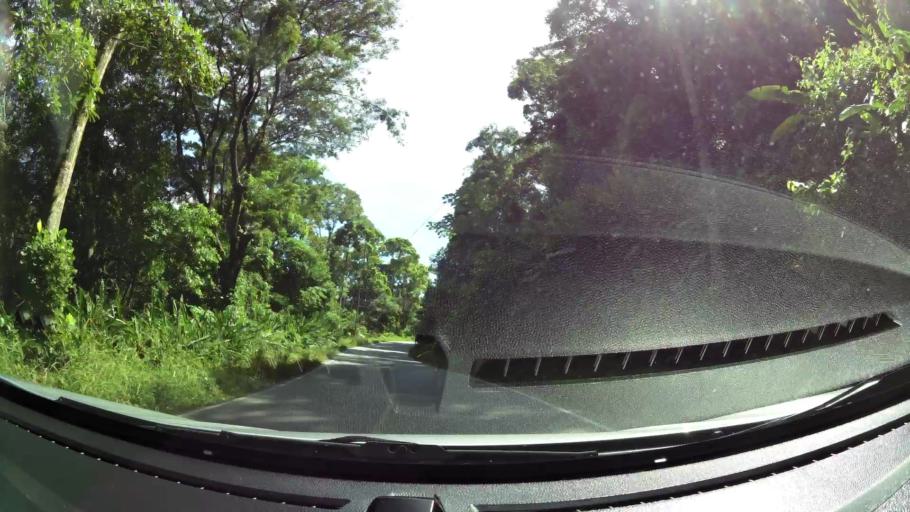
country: CR
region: San Jose
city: San Isidro
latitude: 9.2647
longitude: -83.8634
